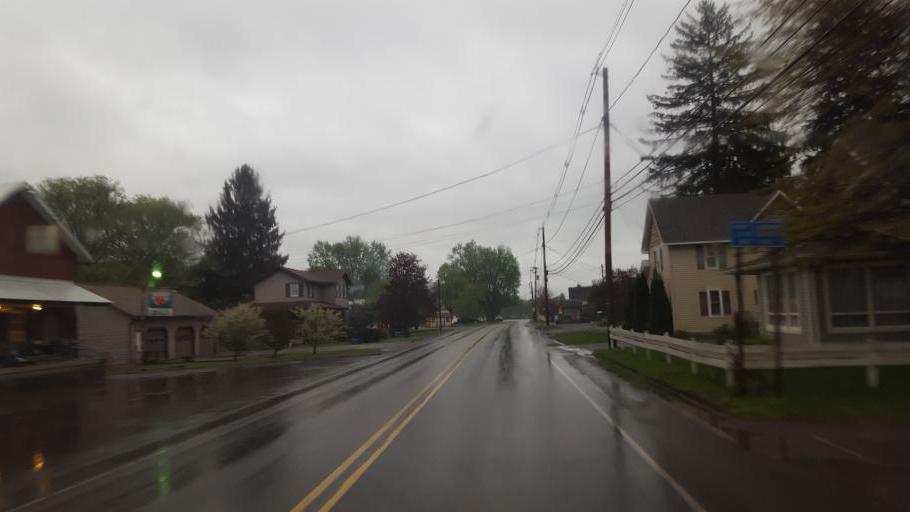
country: US
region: Pennsylvania
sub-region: Tioga County
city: Westfield
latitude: 41.9228
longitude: -77.5296
